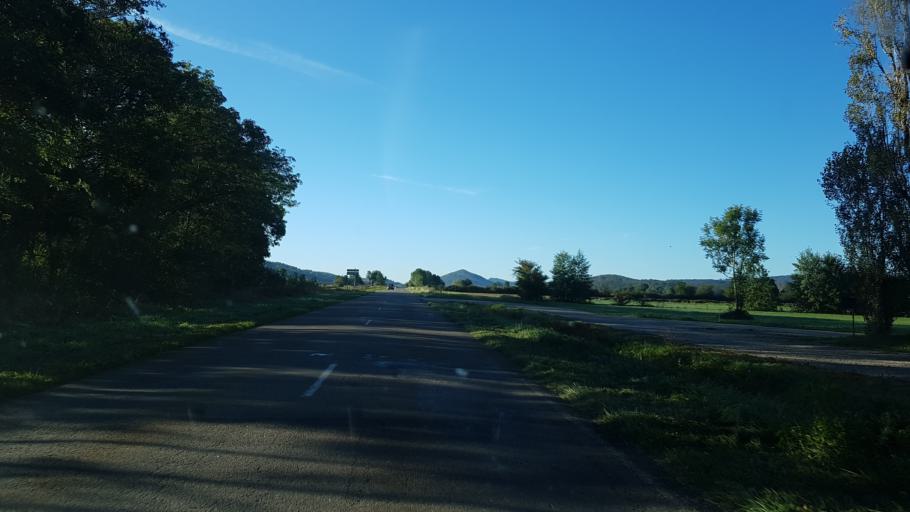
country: FR
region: Bourgogne
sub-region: Departement de Saone-et-Loire
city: Cuiseaux
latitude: 46.4831
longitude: 5.4659
